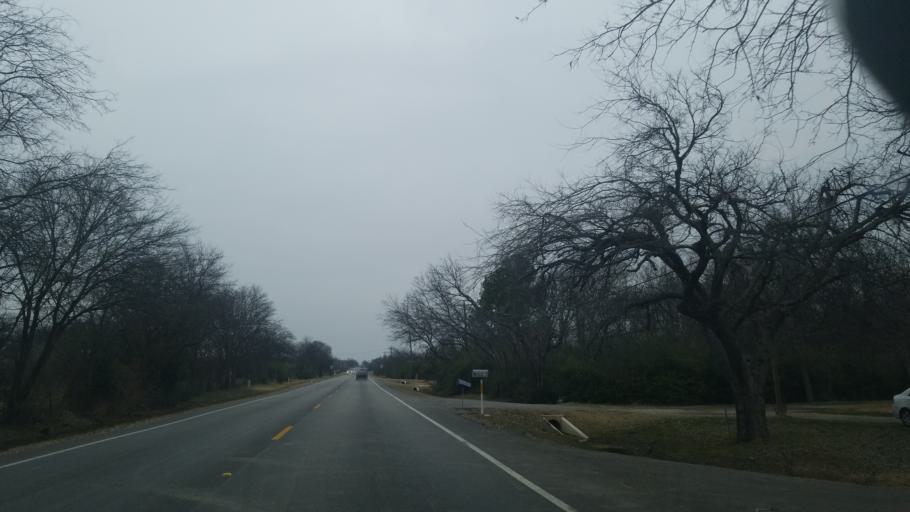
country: US
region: Texas
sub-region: Denton County
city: Denton
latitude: 33.1641
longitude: -97.1419
